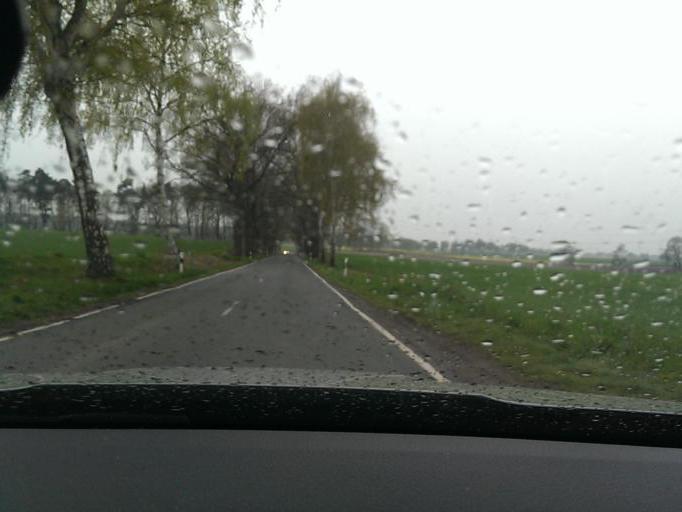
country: DE
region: Lower Saxony
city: Steimbke
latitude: 52.6058
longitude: 9.4712
